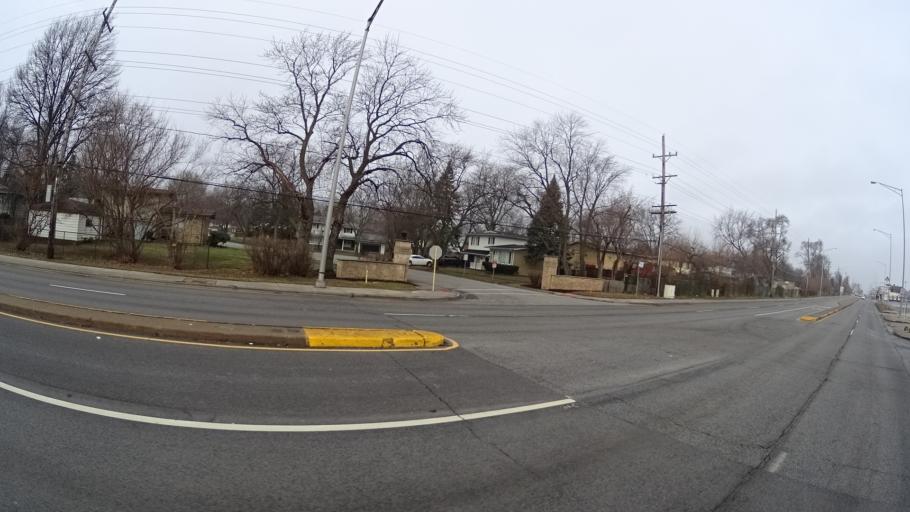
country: US
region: Illinois
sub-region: Cook County
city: East Hazel Crest
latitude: 41.5526
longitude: -87.6359
